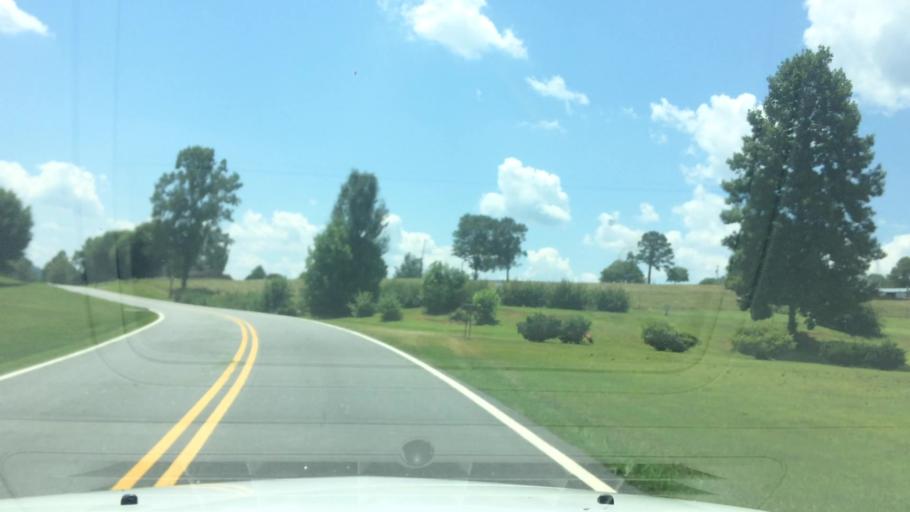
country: US
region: North Carolina
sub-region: Alexander County
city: Taylorsville
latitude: 35.9427
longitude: -81.2685
